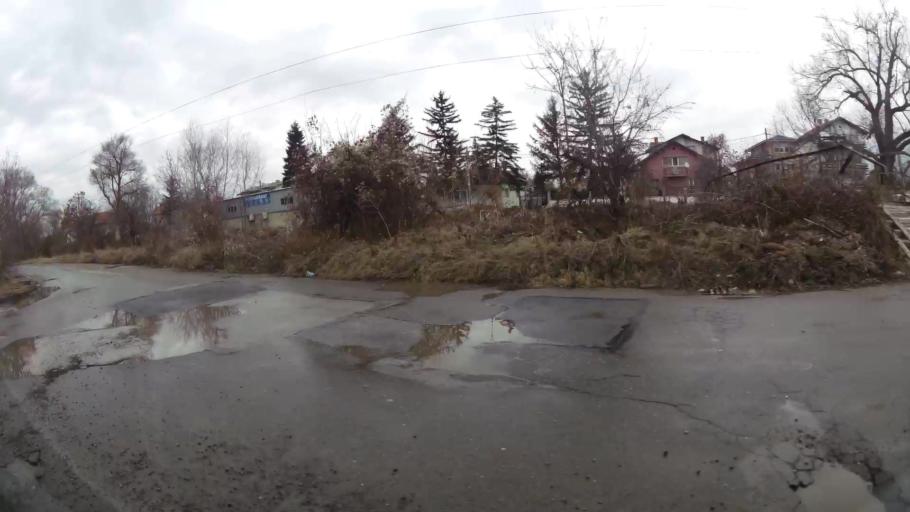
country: BG
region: Sofiya
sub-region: Obshtina Bozhurishte
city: Bozhurishte
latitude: 42.7406
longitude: 23.2677
